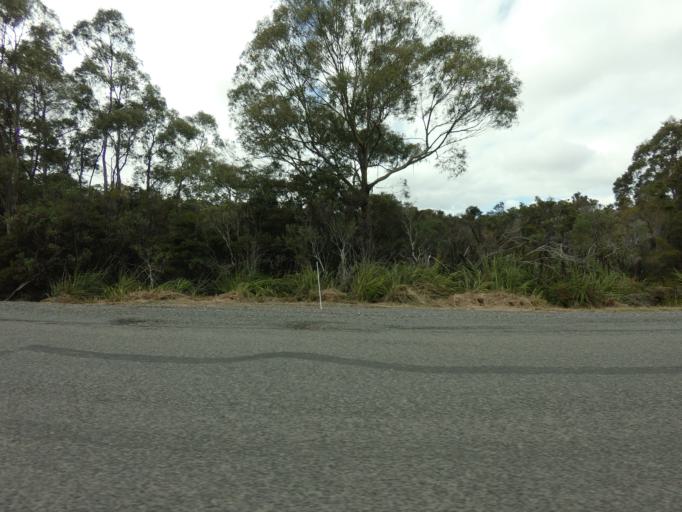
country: AU
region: Tasmania
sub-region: Huon Valley
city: Geeveston
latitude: -43.4225
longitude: 146.9048
